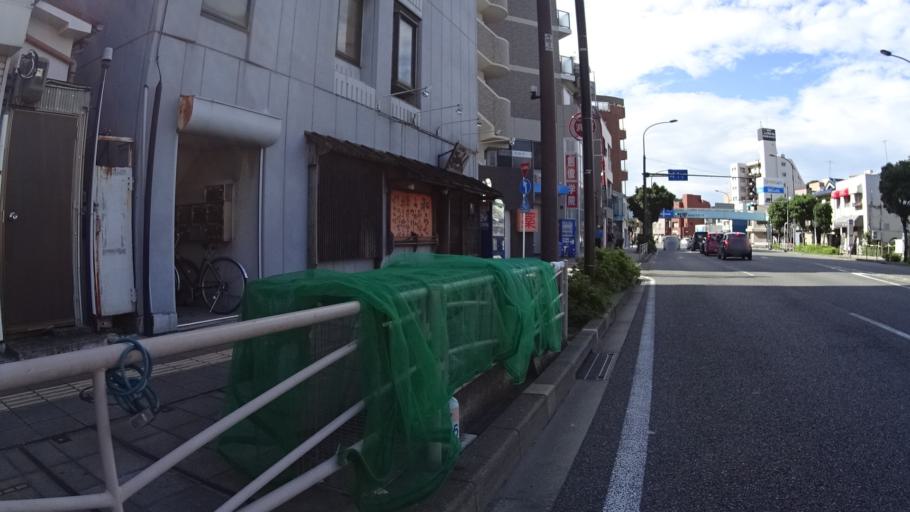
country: JP
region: Kanagawa
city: Yokosuka
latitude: 35.2738
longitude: 139.6770
